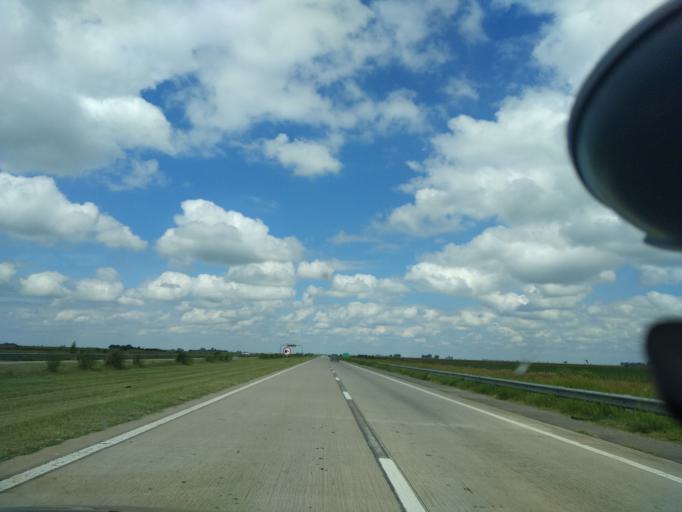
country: AR
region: Cordoba
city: Leones
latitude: -32.5992
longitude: -62.4631
